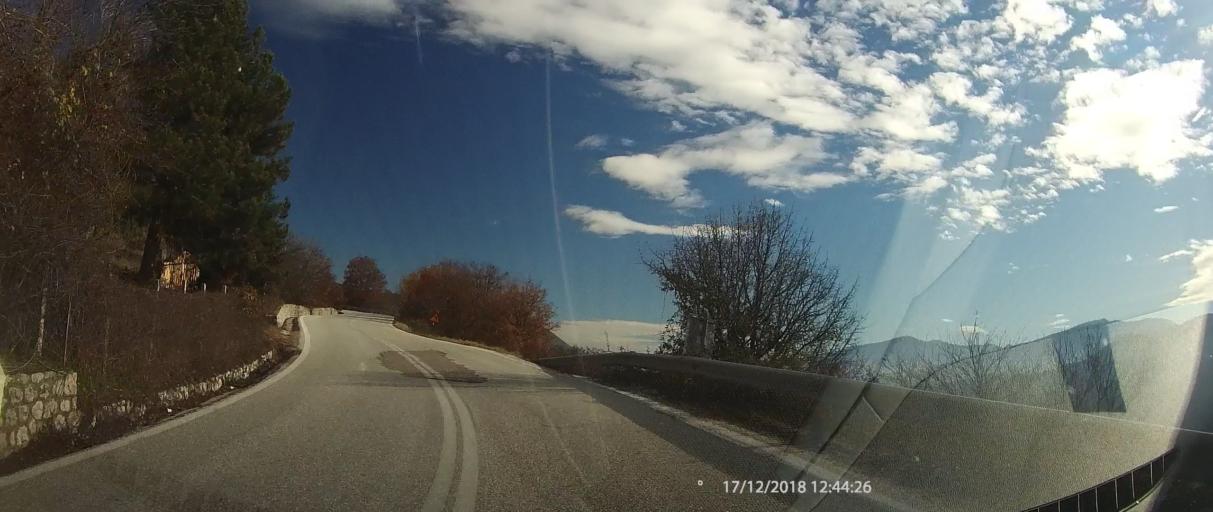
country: GR
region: Epirus
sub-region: Nomos Ioanninon
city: Metsovo
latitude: 39.7839
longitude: 21.3995
